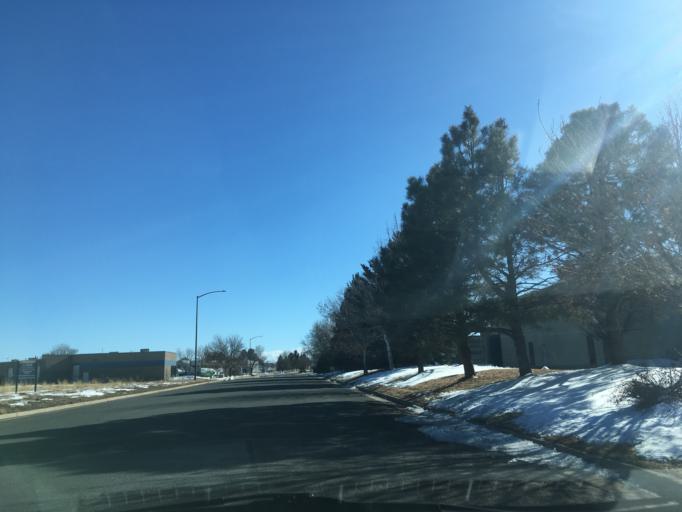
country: US
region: Colorado
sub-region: Boulder County
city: Louisville
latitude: 39.9617
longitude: -105.1219
